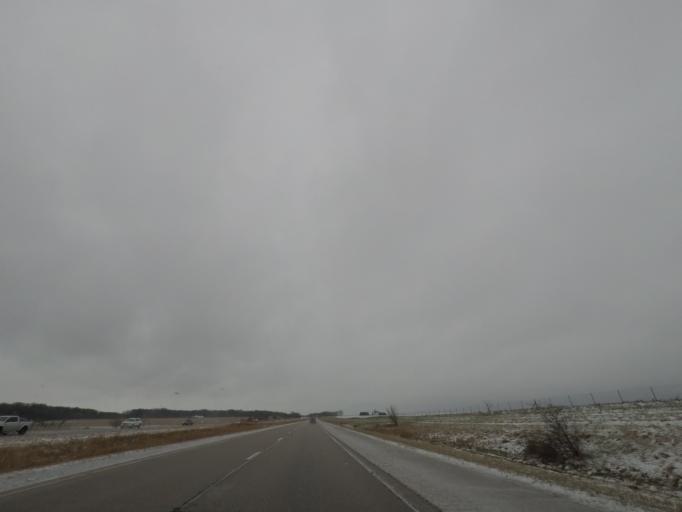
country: US
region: Illinois
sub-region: Logan County
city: Atlanta
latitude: 40.3468
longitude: -89.1283
